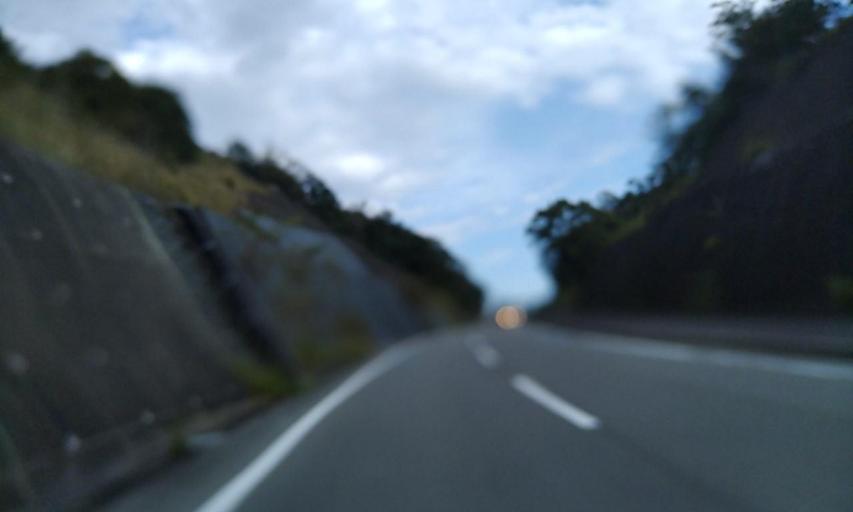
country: JP
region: Mie
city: Ise
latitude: 34.2848
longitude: 136.5501
